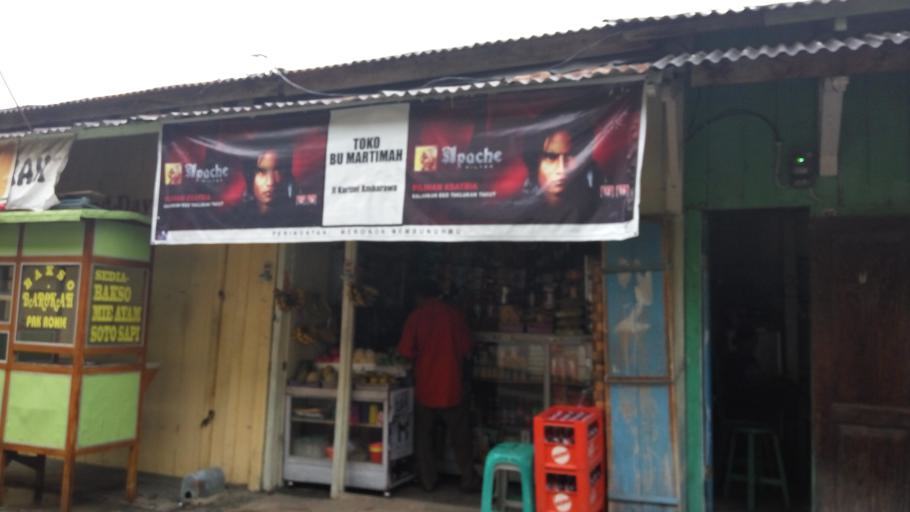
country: ID
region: Central Java
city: Ambarawa
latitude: -7.2678
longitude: 110.4078
